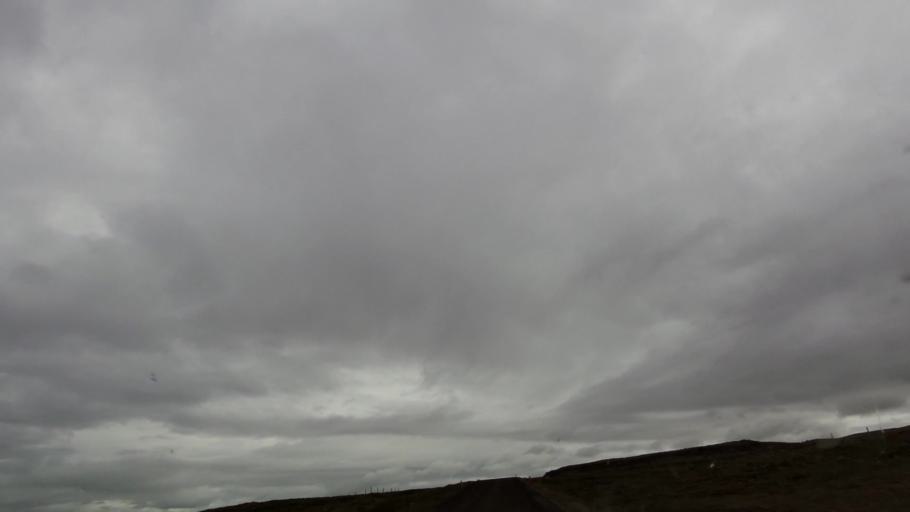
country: IS
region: West
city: Borgarnes
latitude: 65.0240
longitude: -22.1049
